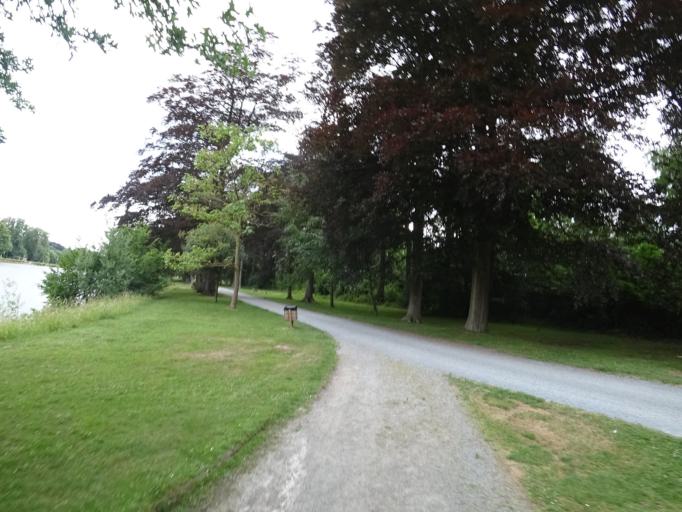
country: BE
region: Wallonia
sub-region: Province du Hainaut
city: Enghien
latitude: 50.6924
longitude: 4.0454
